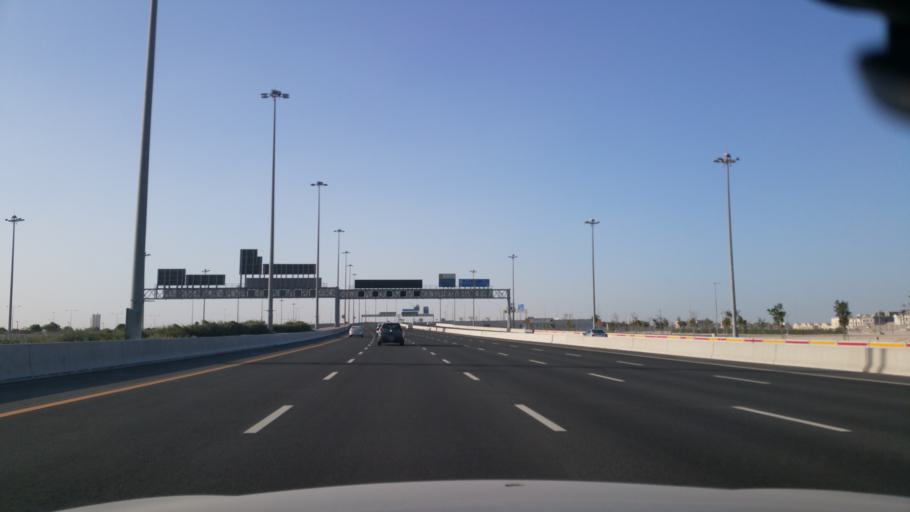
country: QA
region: Al Wakrah
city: Al Wukayr
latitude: 25.2134
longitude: 51.5381
